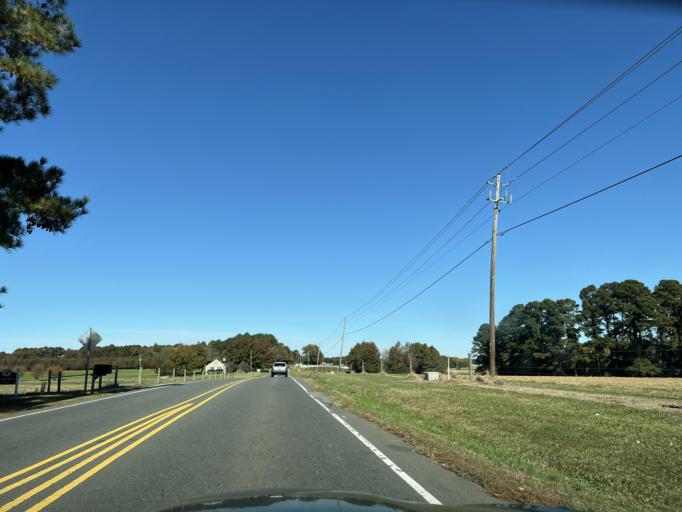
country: US
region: North Carolina
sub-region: Wake County
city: West Raleigh
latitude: 35.7316
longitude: -78.6827
